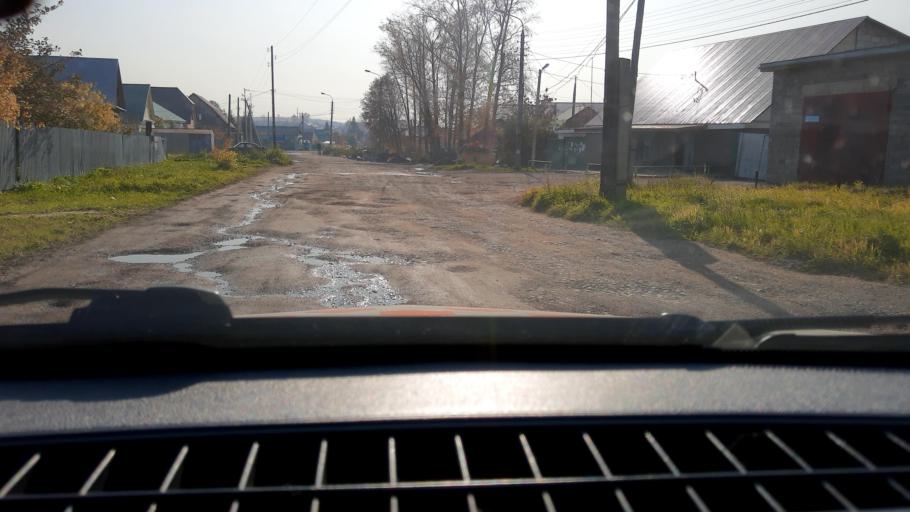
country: RU
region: Bashkortostan
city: Ufa
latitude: 54.8425
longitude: 56.1549
